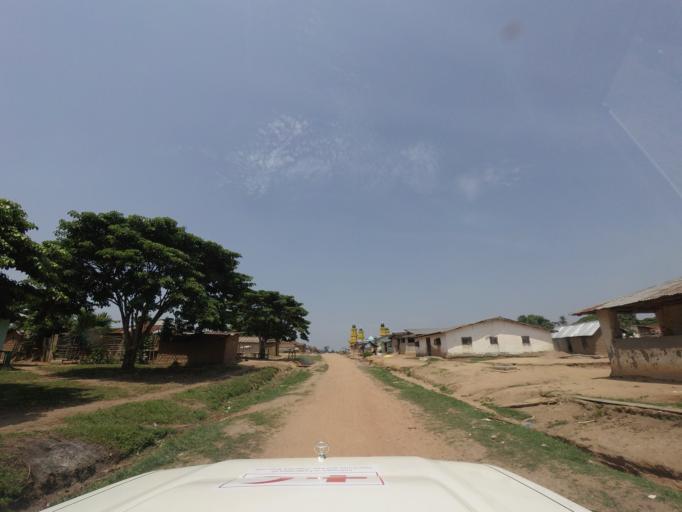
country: LR
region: Lofa
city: Voinjama
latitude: 8.4648
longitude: -9.6677
